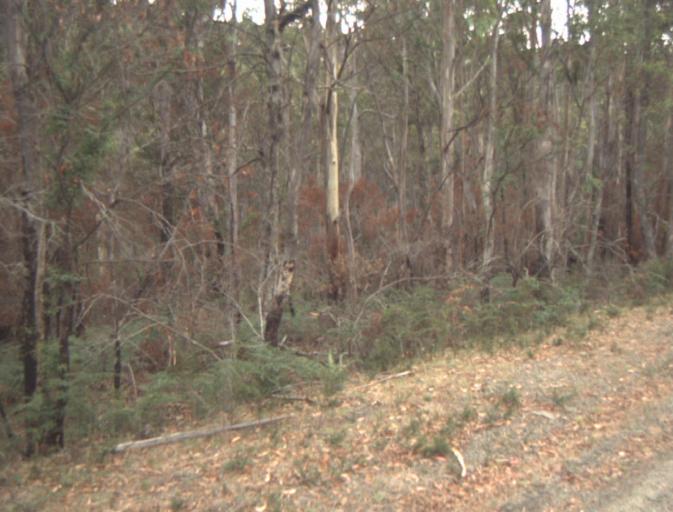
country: AU
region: Tasmania
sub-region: Dorset
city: Scottsdale
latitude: -41.4469
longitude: 147.5221
